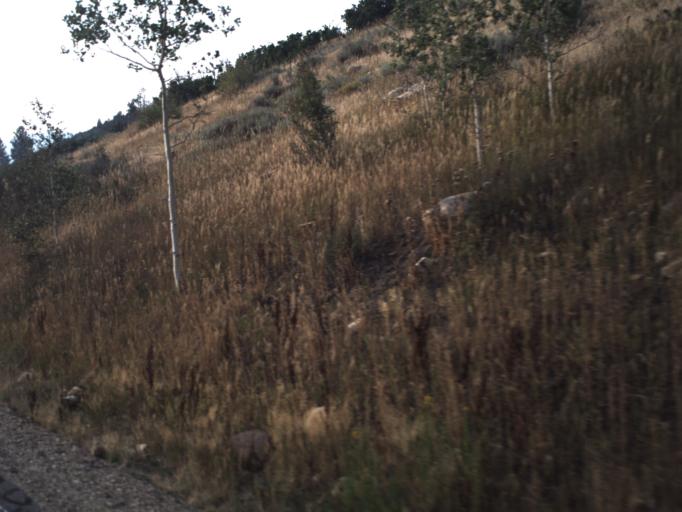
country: US
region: Utah
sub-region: Summit County
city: Francis
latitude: 40.6233
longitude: -111.1538
